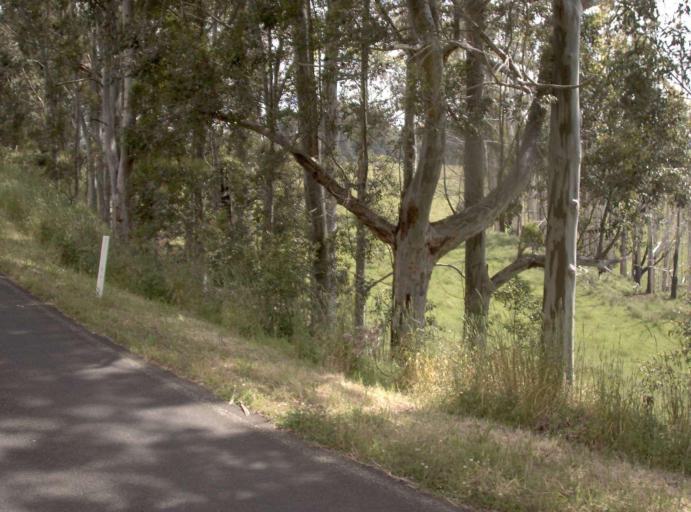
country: AU
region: Victoria
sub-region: Latrobe
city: Traralgon
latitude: -38.3500
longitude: 146.5688
